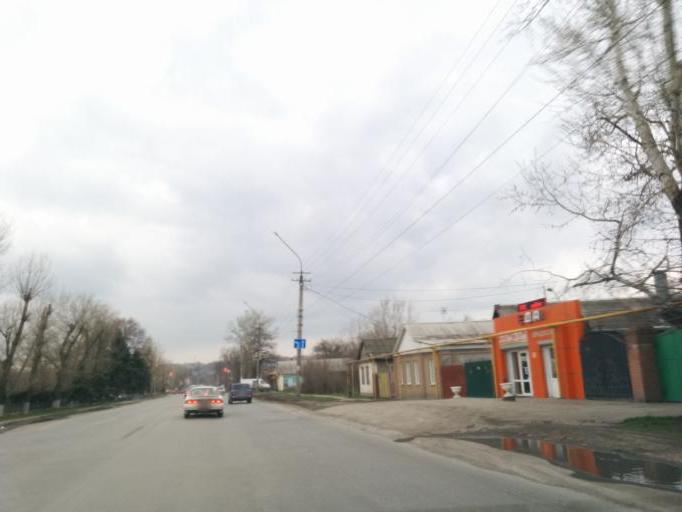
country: RU
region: Rostov
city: Novocherkassk
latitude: 47.4419
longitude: 40.1031
